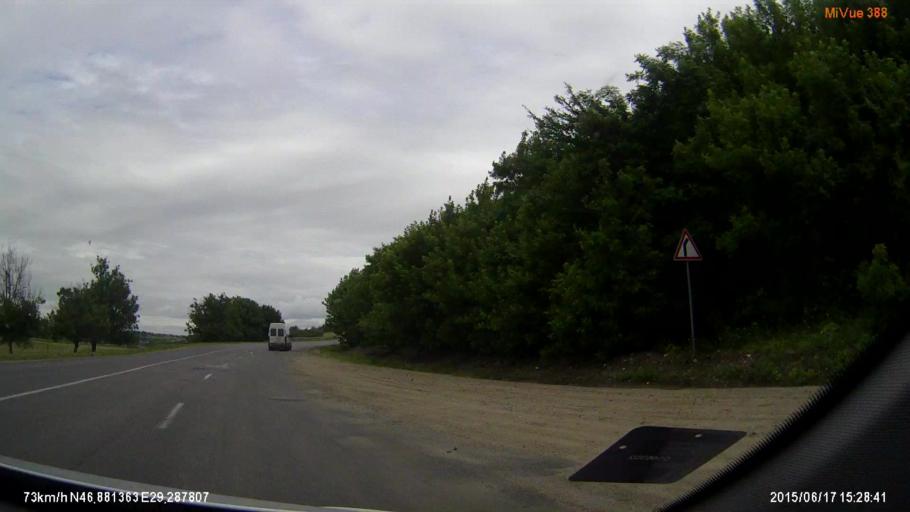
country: MD
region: Anenii Noi
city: Anenii Noi
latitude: 46.8812
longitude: 29.2875
